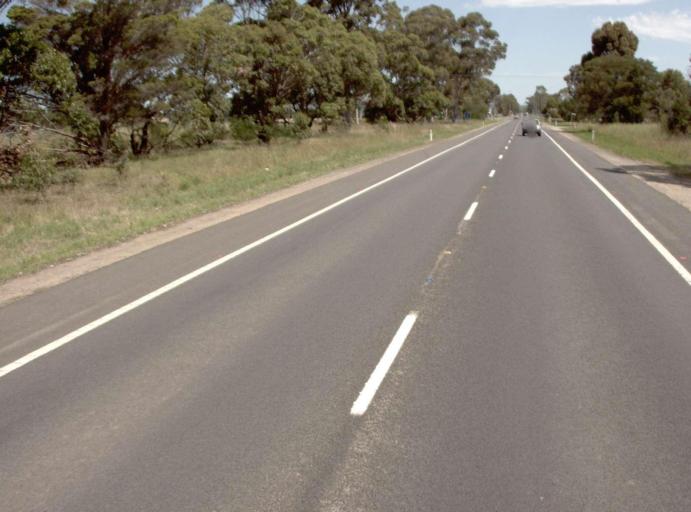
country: AU
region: Victoria
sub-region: Wellington
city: Sale
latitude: -38.0830
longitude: 147.0710
